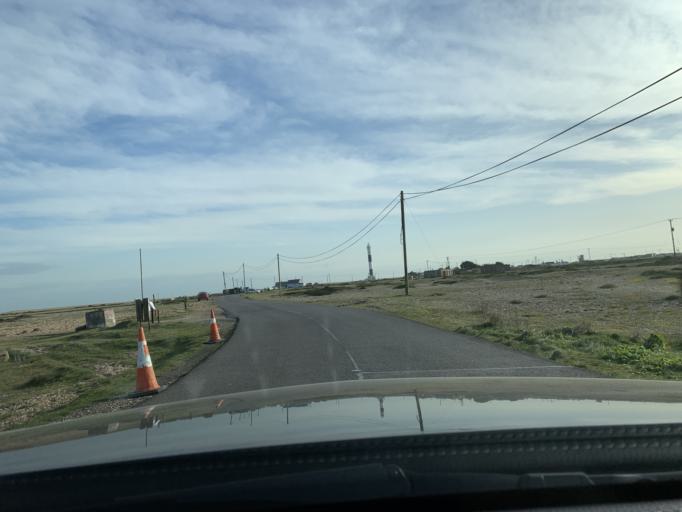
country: GB
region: England
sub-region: Kent
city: New Romney
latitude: 50.9185
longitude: 0.9767
